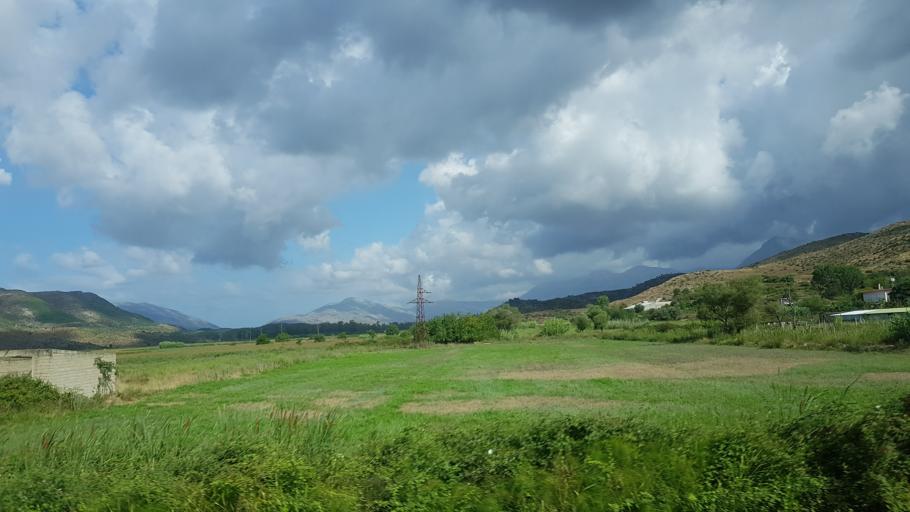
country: AL
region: Vlore
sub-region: Rrethi i Delvines
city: Mesopotam
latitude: 39.9087
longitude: 20.0896
